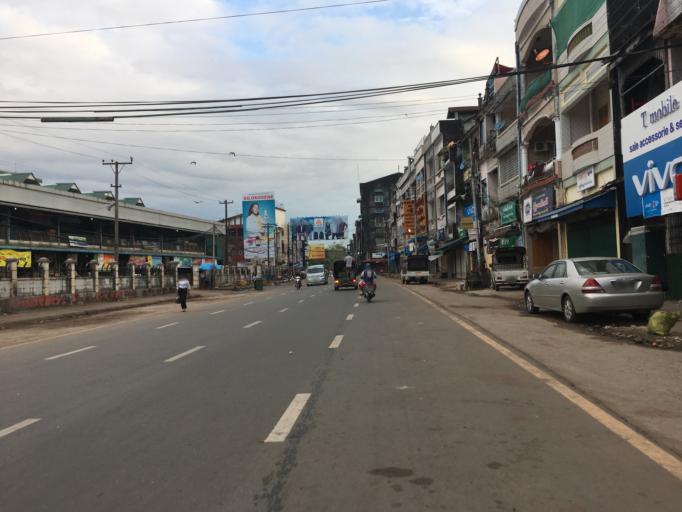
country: MM
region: Mon
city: Mawlamyine
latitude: 16.4940
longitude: 97.6191
